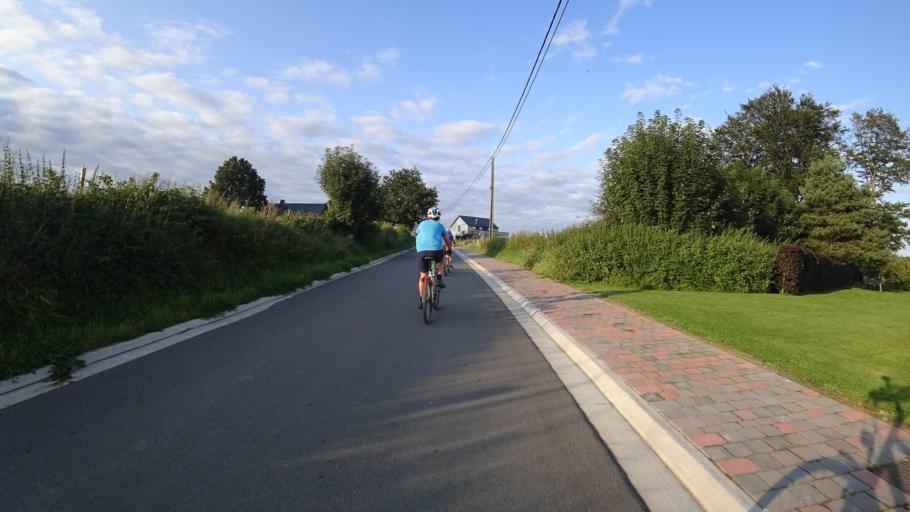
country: BE
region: Wallonia
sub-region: Province du Luxembourg
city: Neufchateau
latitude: 49.8917
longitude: 5.3851
